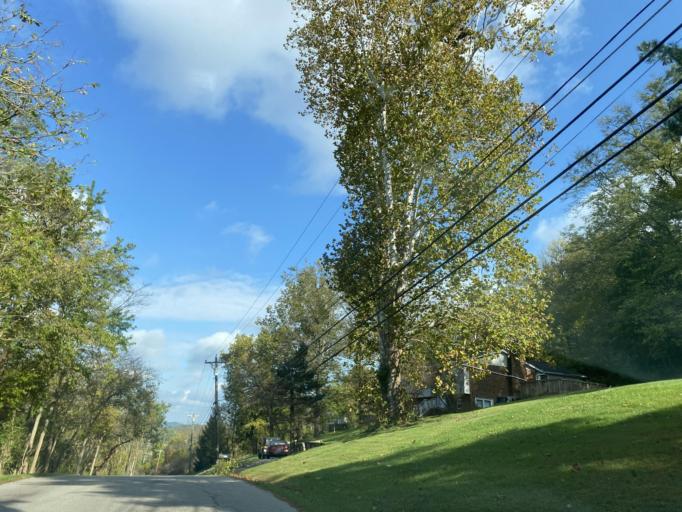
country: US
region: Kentucky
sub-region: Campbell County
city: Cold Spring
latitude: 39.0369
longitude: -84.4199
